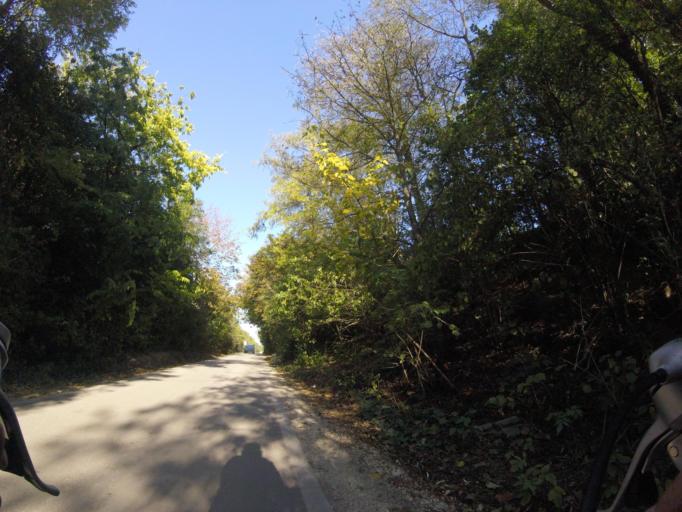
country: HU
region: Fejer
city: Bicske
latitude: 47.4958
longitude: 18.6506
